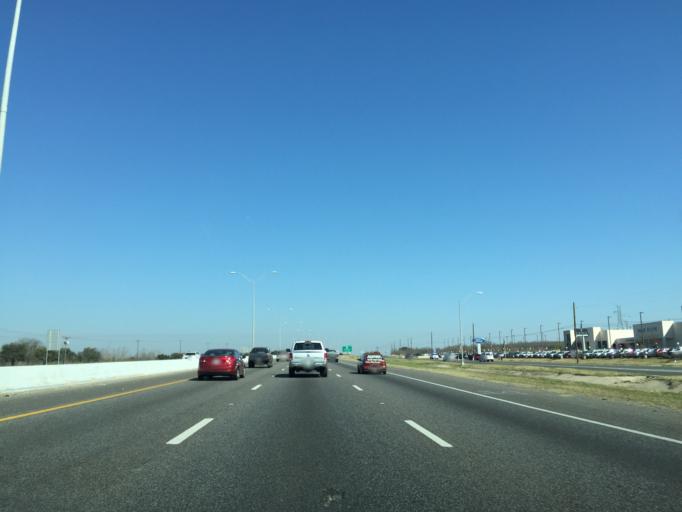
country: US
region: Texas
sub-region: Williamson County
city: Georgetown
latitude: 30.5811
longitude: -97.6928
